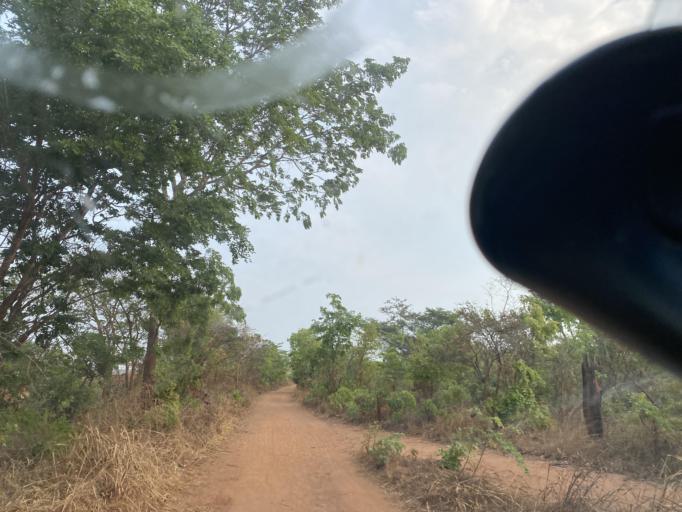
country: ZM
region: Lusaka
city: Chongwe
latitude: -15.1967
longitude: 28.4928
